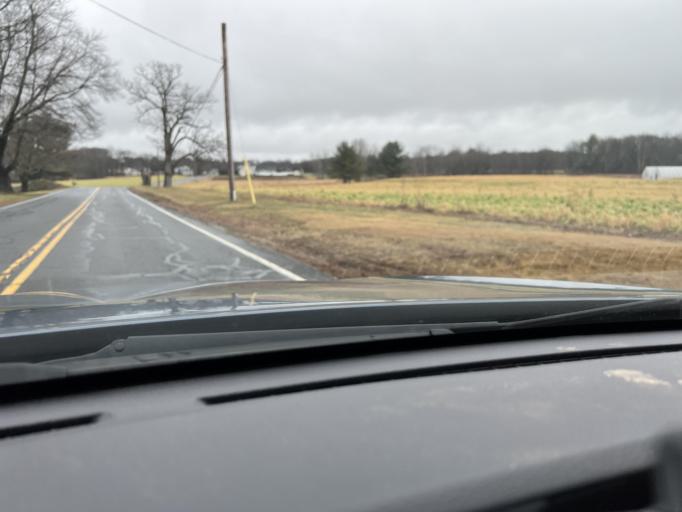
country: US
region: Massachusetts
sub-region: Hampden County
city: Southwick
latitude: 42.0373
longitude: -72.7103
